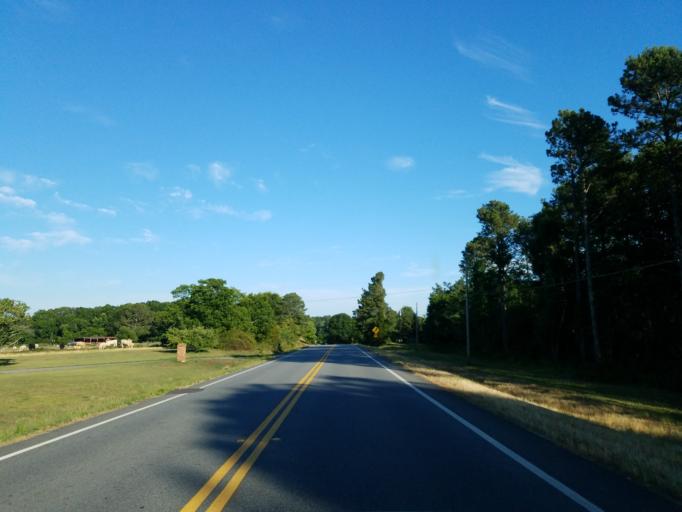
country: US
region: Georgia
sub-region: Gordon County
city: Calhoun
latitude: 34.5514
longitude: -85.0051
